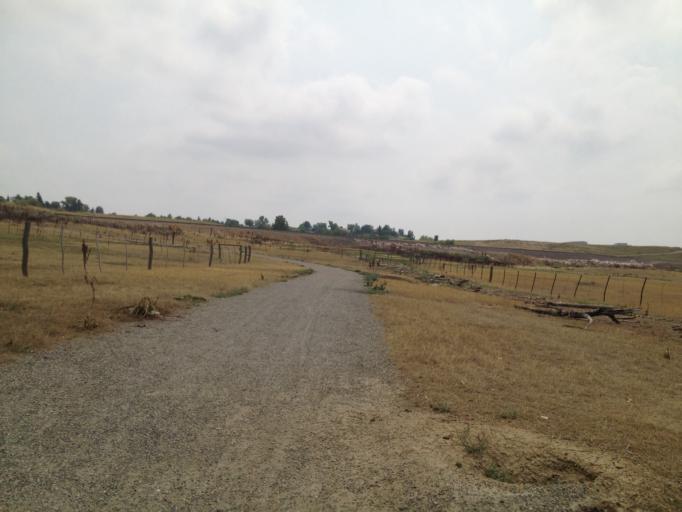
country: US
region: Colorado
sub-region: Broomfield County
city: Broomfield
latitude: 39.9369
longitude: -105.1093
